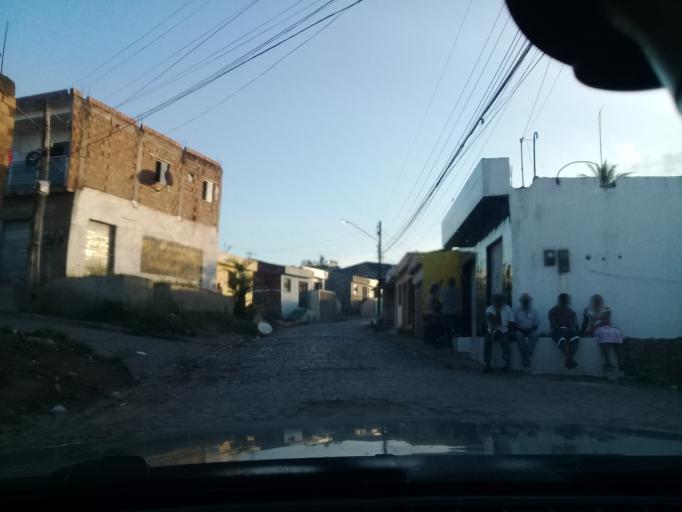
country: BR
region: Pernambuco
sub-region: Vitoria De Santo Antao
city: Vitoria de Santo Antao
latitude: -8.1266
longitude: -35.2830
